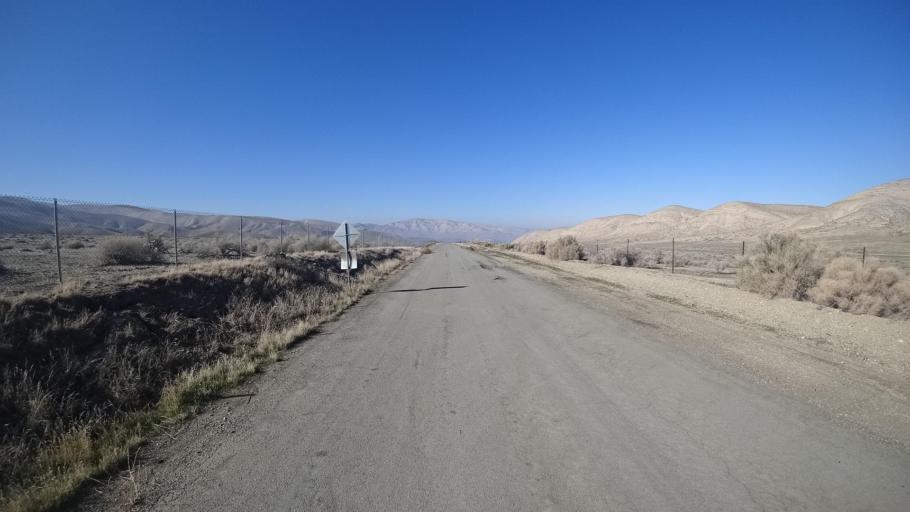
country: US
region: California
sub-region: Kern County
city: Maricopa
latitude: 34.9940
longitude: -119.3932
